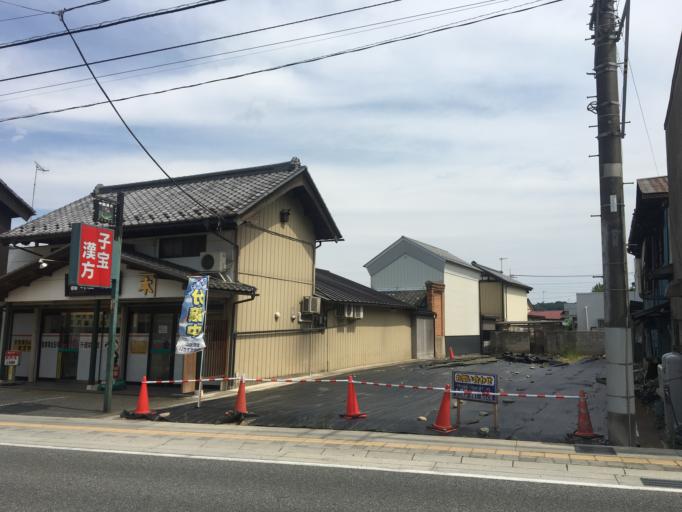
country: JP
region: Saitama
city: Yorii
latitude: 36.1151
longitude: 139.1954
